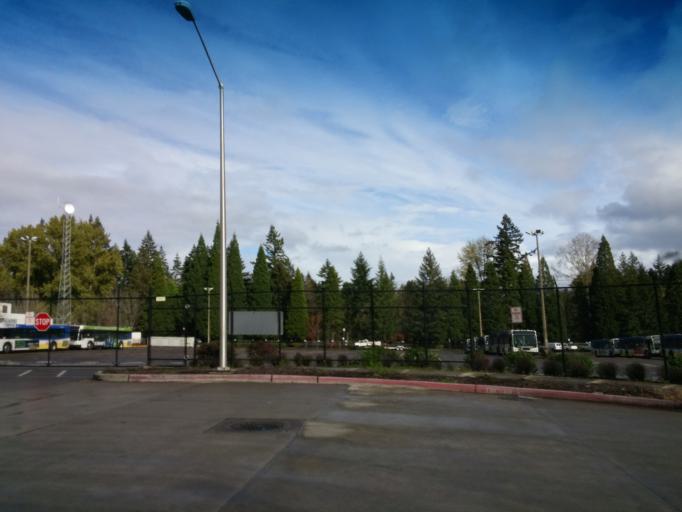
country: US
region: Oregon
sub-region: Washington County
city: Aloha
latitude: 45.5040
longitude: -122.8446
